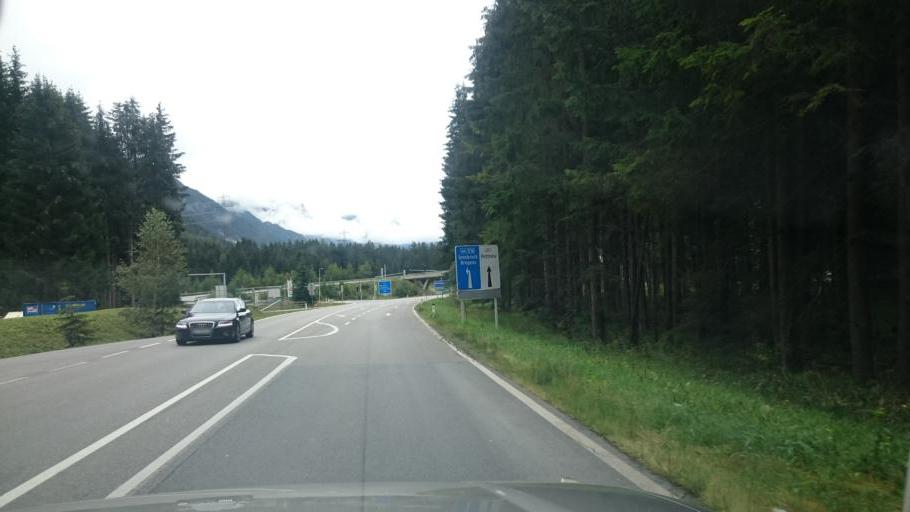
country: AT
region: Tyrol
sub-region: Politischer Bezirk Landeck
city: Sankt Anton am Arlberg
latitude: 47.1435
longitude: 10.3115
